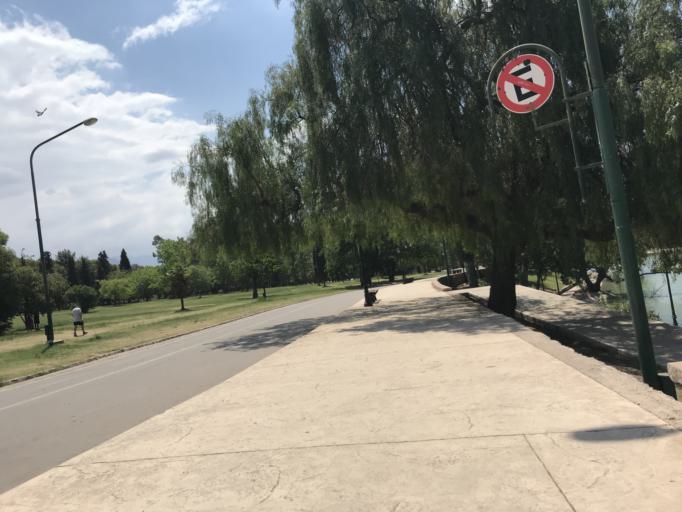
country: AR
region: Mendoza
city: Mendoza
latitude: -32.8975
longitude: -68.8653
